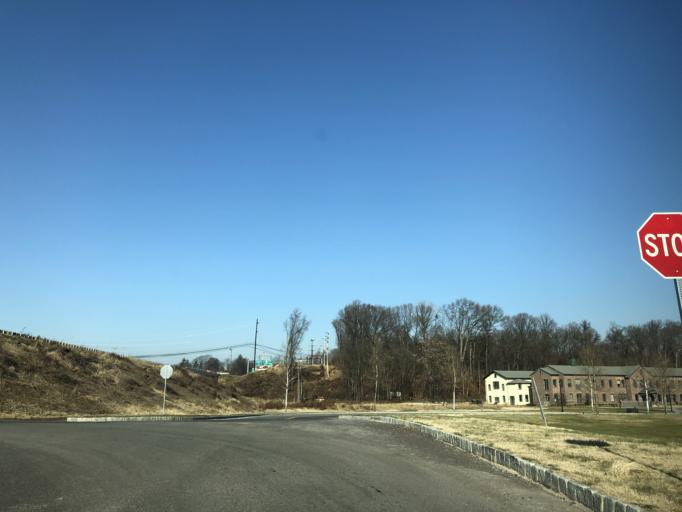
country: US
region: Pennsylvania
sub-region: Montgomery County
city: Audubon
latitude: 40.1089
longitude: -75.4190
